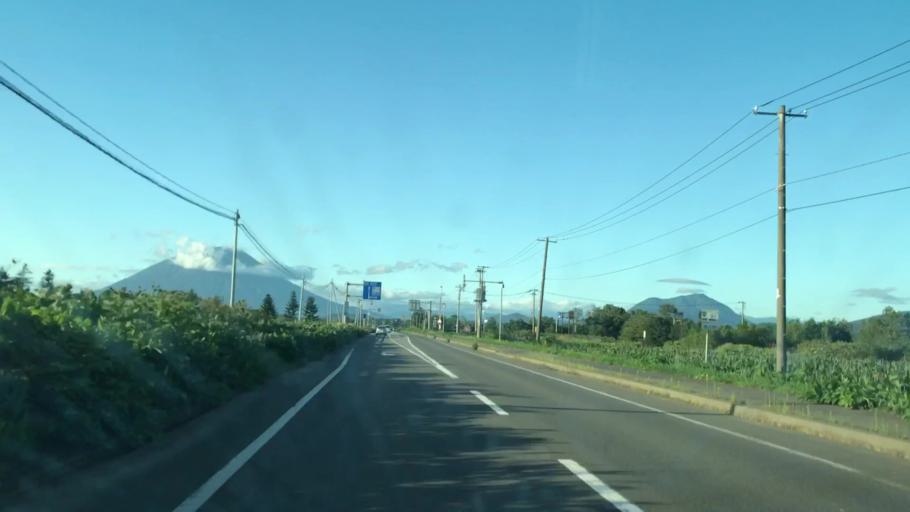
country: JP
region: Hokkaido
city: Date
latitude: 42.6413
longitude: 140.8031
